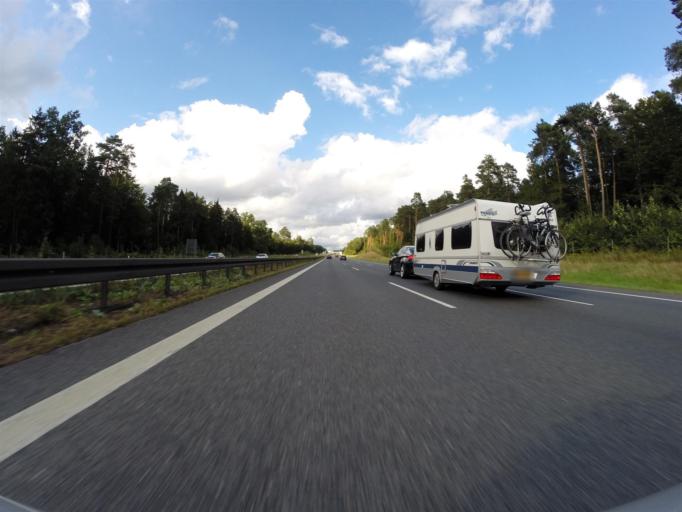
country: DE
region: Bavaria
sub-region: Regierungsbezirk Mittelfranken
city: Schwaig
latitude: 49.4248
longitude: 11.2088
